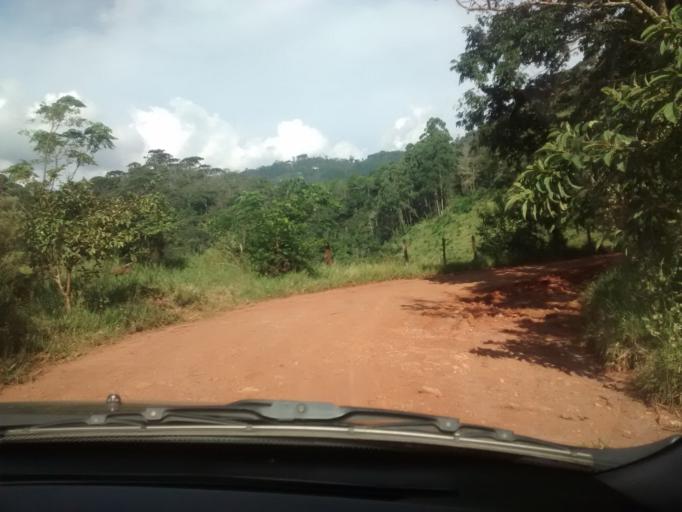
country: BR
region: Sao Paulo
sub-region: Campos Do Jordao
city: Campos do Jordao
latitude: -22.7379
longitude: -45.6694
